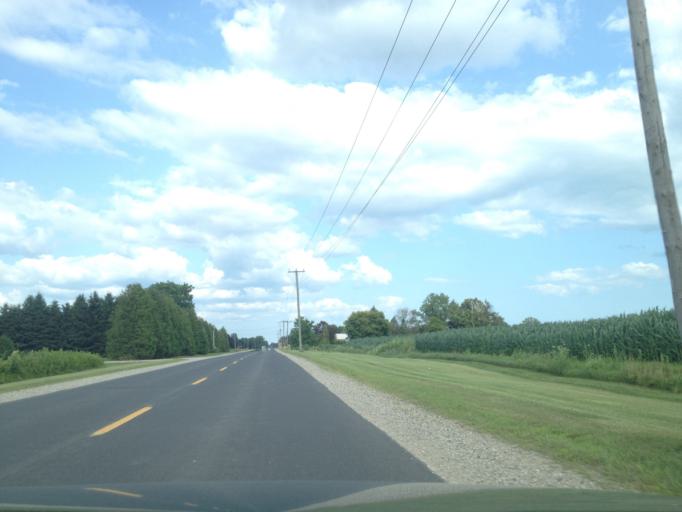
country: CA
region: Ontario
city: Aylmer
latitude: 42.6755
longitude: -80.9667
